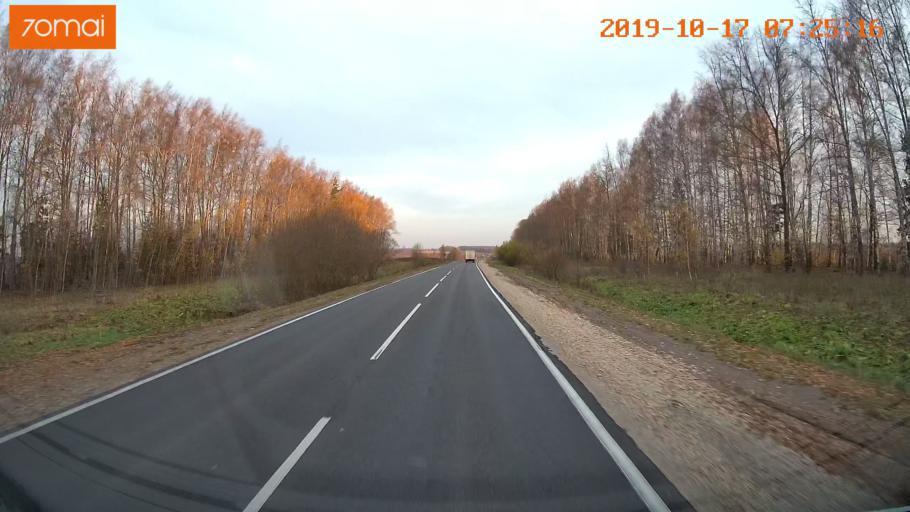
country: RU
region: Ivanovo
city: Gavrilov Posad
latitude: 56.3482
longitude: 40.1075
